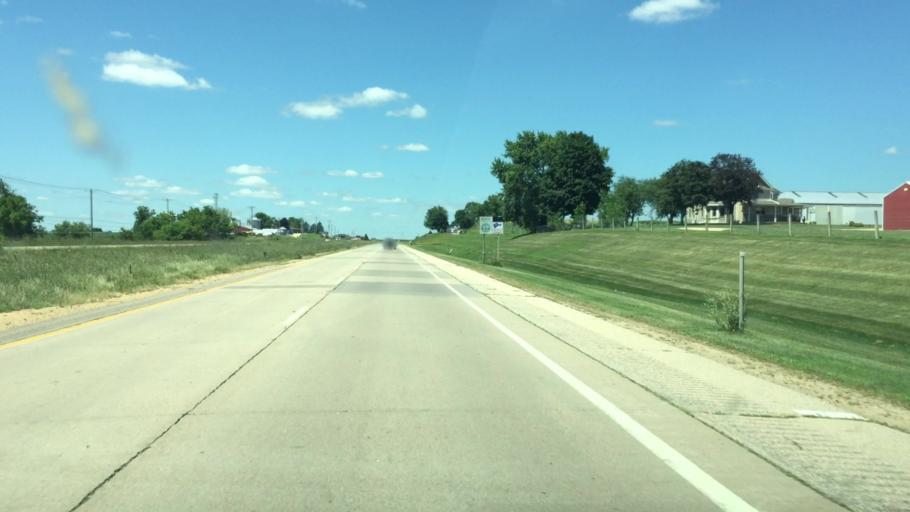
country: US
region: Wisconsin
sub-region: Grant County
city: Dickeyville
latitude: 42.5629
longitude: -90.6108
